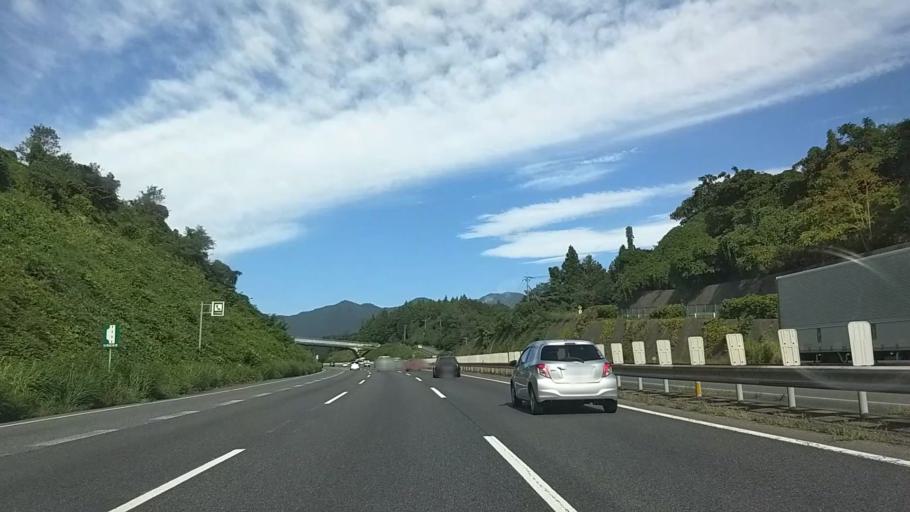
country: JP
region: Yamanashi
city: Uenohara
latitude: 35.6319
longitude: 139.0969
